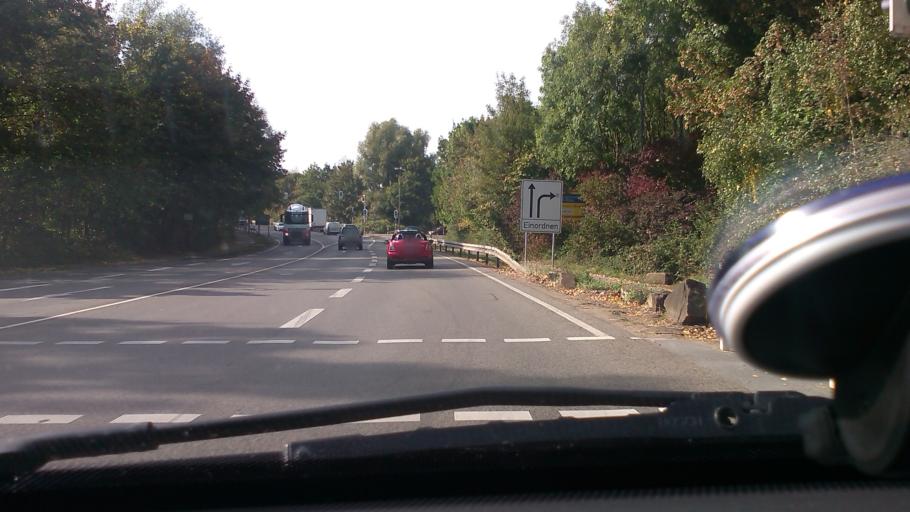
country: DE
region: North Rhine-Westphalia
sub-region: Regierungsbezirk Dusseldorf
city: Langenfeld
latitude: 51.1279
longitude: 6.9565
